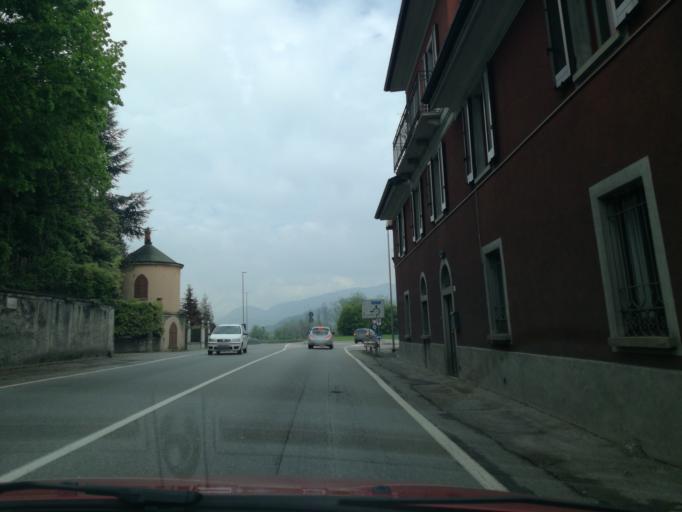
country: IT
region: Lombardy
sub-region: Provincia di Lecco
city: Canova-San Zeno
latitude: 45.7103
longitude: 9.4068
